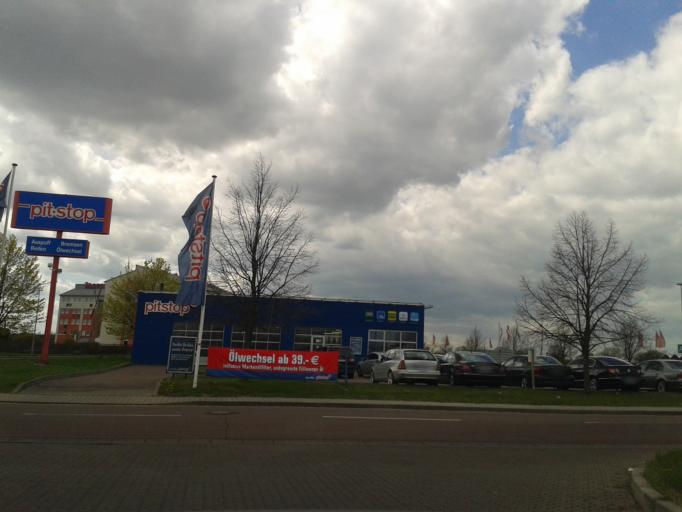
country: DE
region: Saxony-Anhalt
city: Peissen
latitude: 51.5097
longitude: 12.0523
